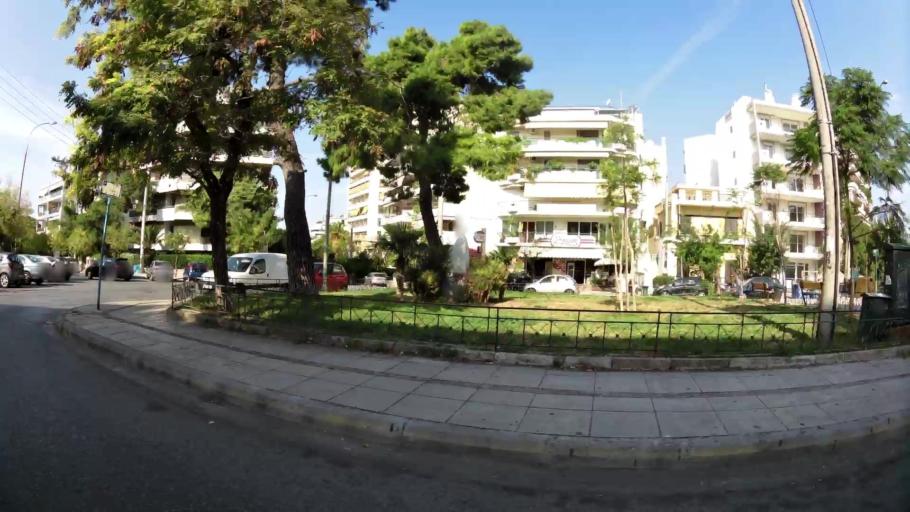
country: GR
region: Attica
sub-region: Nomarchia Athinas
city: Galatsi
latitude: 38.0174
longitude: 23.7412
